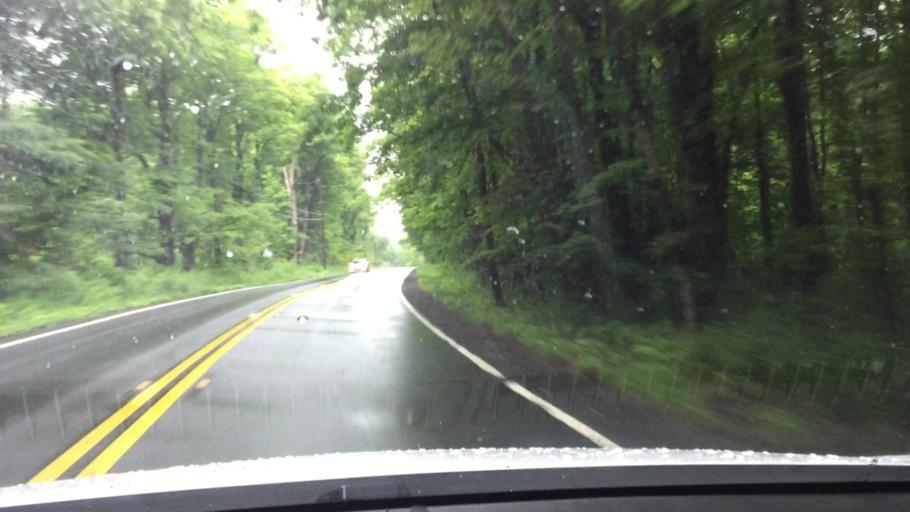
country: US
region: Massachusetts
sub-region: Berkshire County
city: Becket
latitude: 42.3378
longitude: -73.1086
